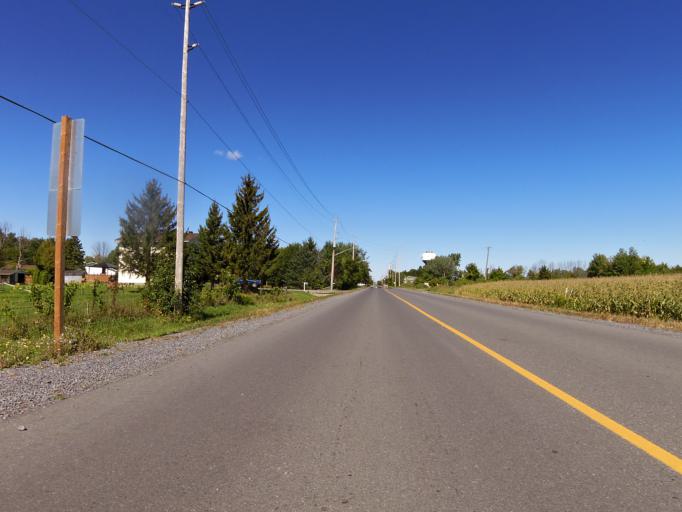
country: CA
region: Ontario
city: Casselman
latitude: 45.2659
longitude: -75.2707
